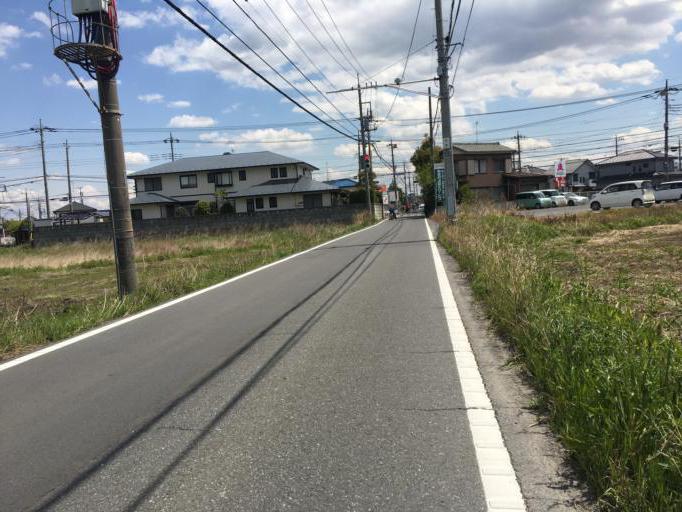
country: JP
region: Saitama
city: Kawagoe
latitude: 35.9325
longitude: 139.4732
